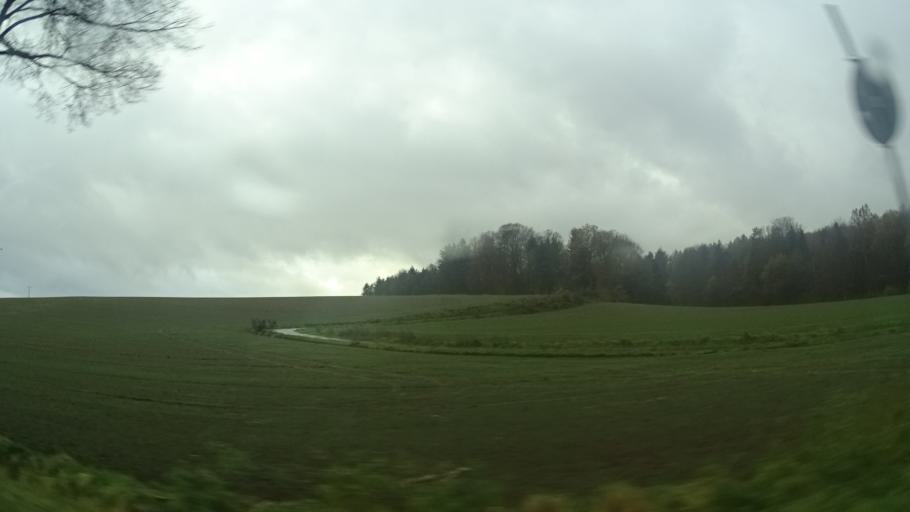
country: DE
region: Hesse
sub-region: Regierungsbezirk Kassel
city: Eichenzell
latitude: 50.4803
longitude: 9.6549
